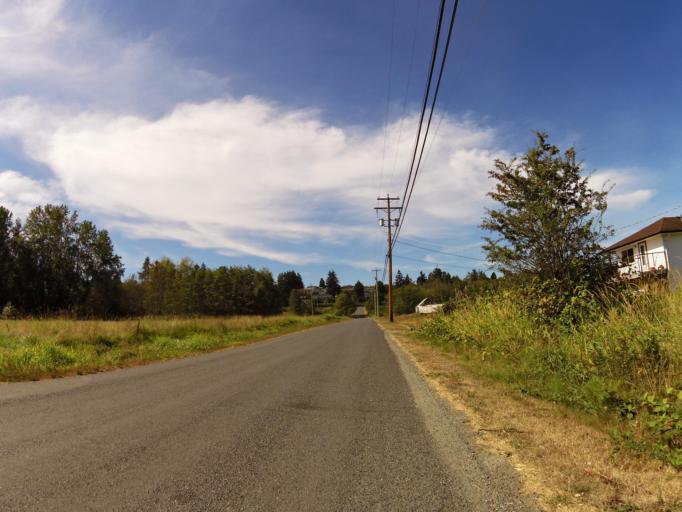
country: CA
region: British Columbia
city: North Saanich
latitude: 48.5616
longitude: -123.3899
